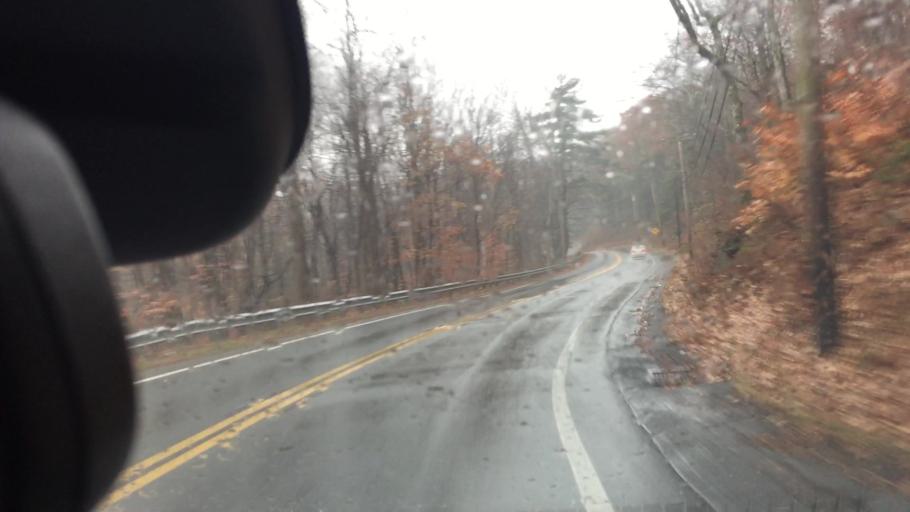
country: US
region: Massachusetts
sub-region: Hampden County
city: Granville
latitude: 42.1713
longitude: -72.9058
